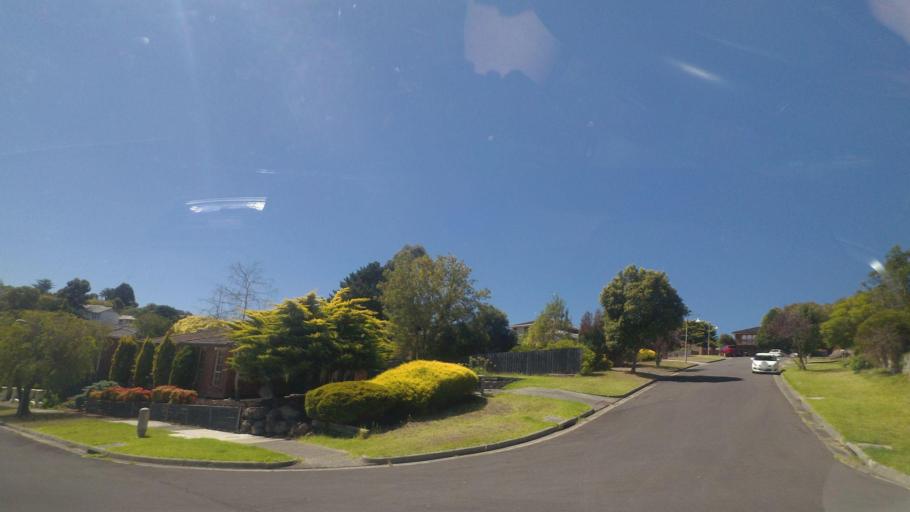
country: AU
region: Victoria
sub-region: Manningham
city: Donvale
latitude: -37.7688
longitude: 145.1772
